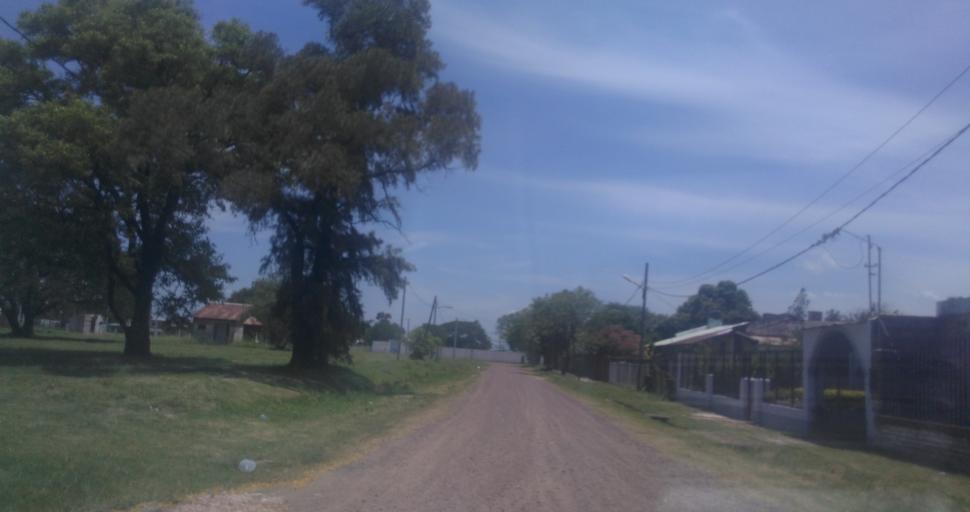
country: AR
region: Chaco
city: Fontana
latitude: -27.4168
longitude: -59.0341
